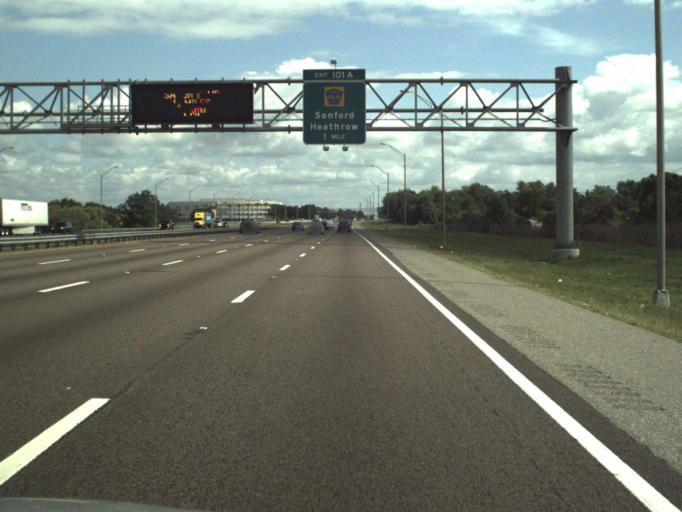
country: US
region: Florida
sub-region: Seminole County
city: Heathrow
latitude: 28.7667
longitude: -81.3594
